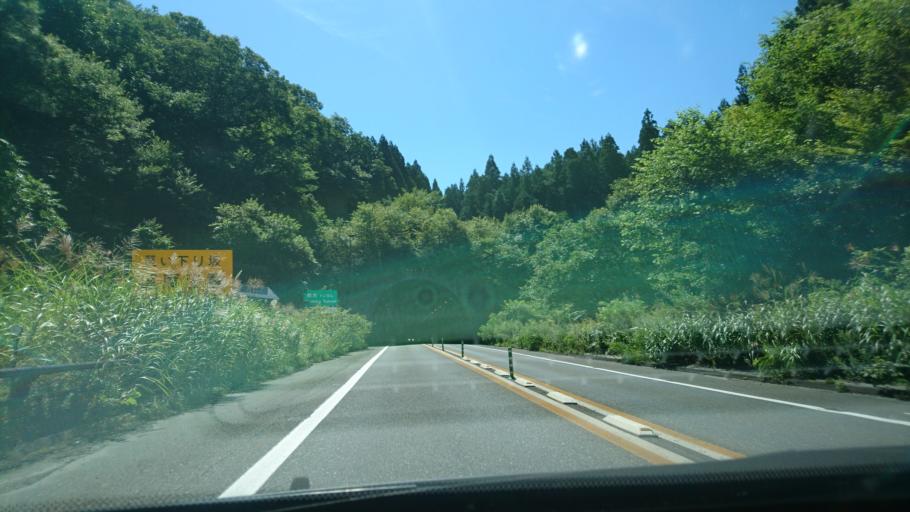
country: JP
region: Iwate
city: Tono
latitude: 39.2559
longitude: 141.6283
